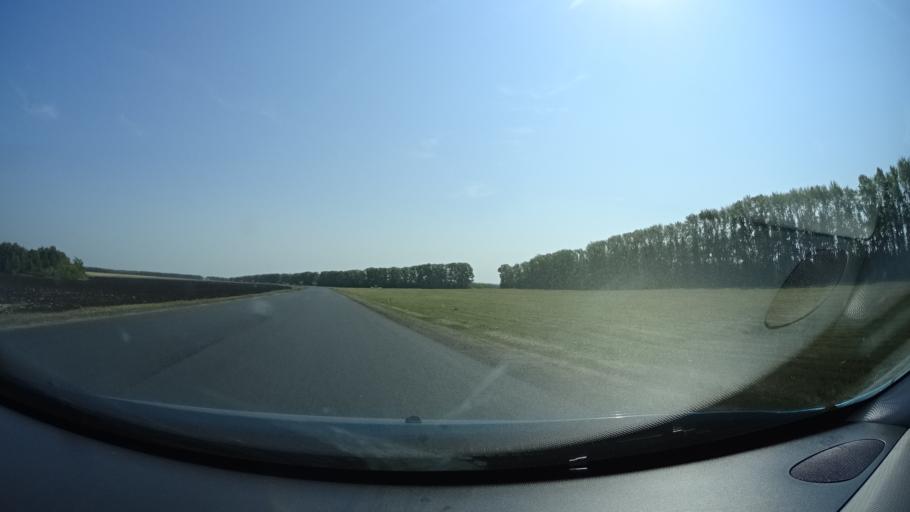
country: RU
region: Bashkortostan
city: Karmaskaly
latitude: 54.3872
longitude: 56.1374
